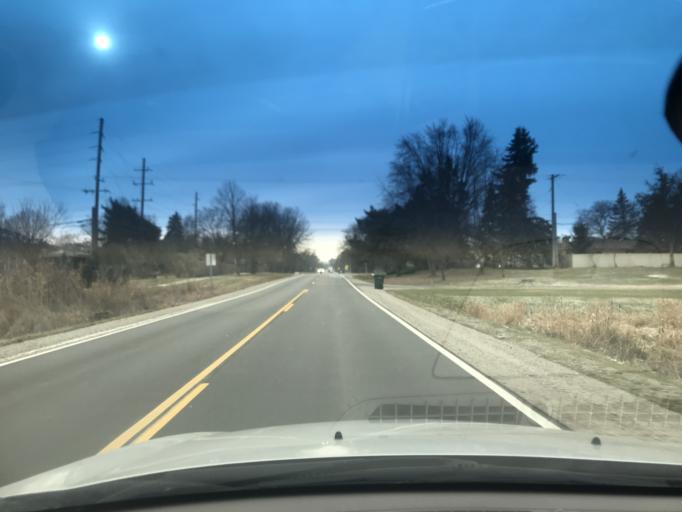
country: US
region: Michigan
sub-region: Macomb County
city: Shelby
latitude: 42.6963
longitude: -83.0545
